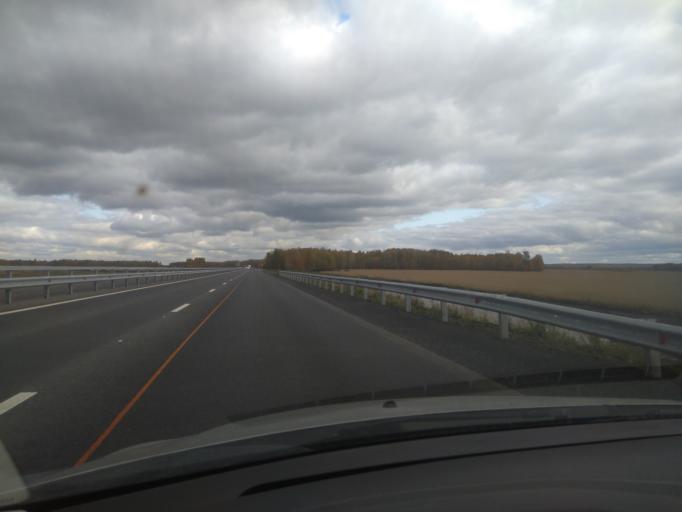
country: RU
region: Sverdlovsk
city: Pyshma
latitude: 56.9016
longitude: 63.0840
